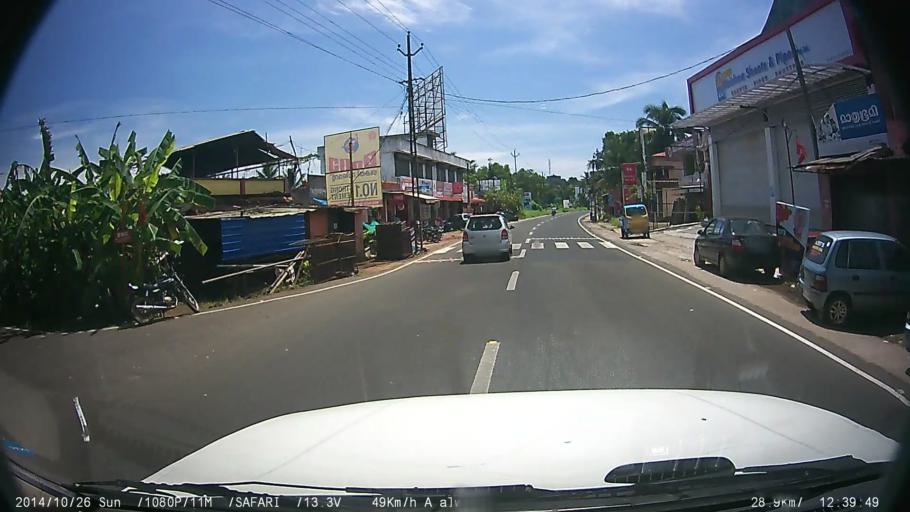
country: IN
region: Kerala
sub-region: Kottayam
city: Kottayam
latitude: 9.5598
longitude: 76.5155
